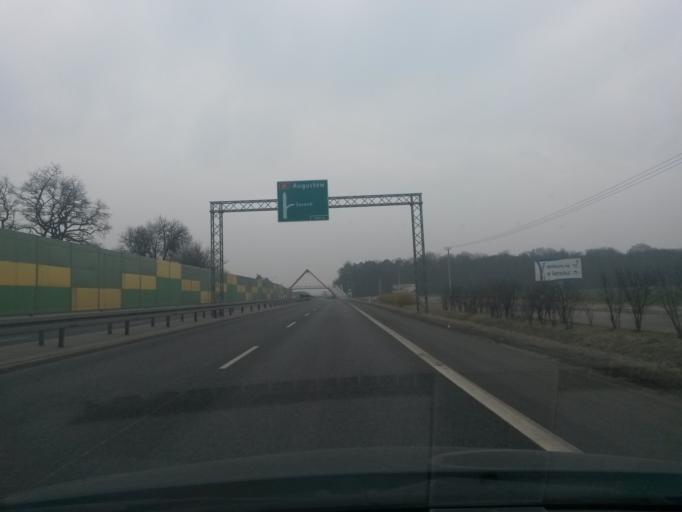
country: PL
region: Masovian Voivodeship
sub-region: Powiat legionowski
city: Serock
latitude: 52.4860
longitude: 21.0436
